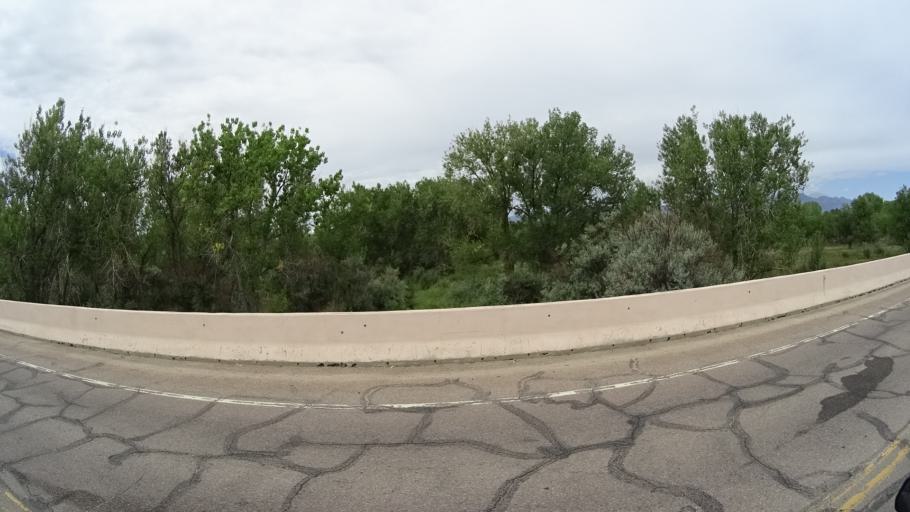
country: US
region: Colorado
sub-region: El Paso County
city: Fountain
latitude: 38.6732
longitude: -104.6965
